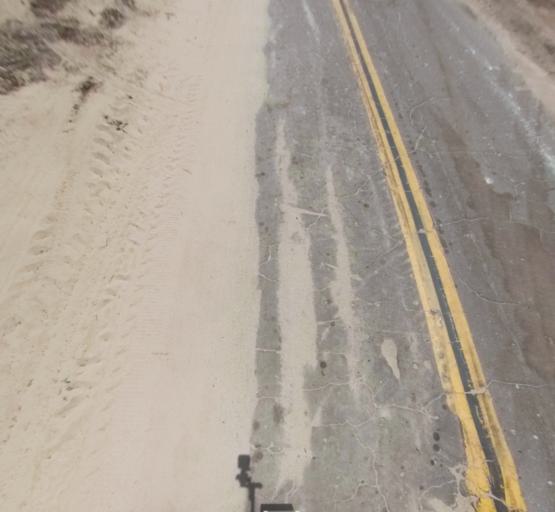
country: US
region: California
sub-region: Fresno County
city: Biola
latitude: 36.8365
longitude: -120.1330
